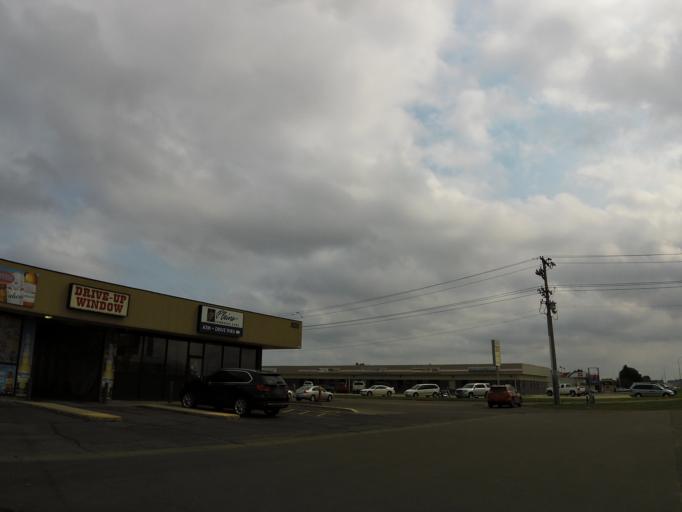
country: US
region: South Dakota
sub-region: Codington County
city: Watertown
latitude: 44.8892
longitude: -97.1088
